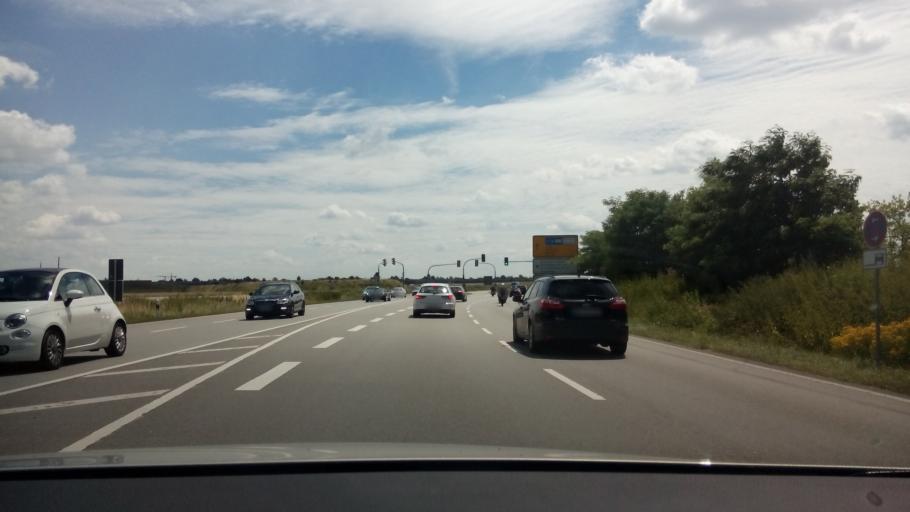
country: DE
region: Bavaria
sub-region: Upper Bavaria
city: Garching bei Munchen
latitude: 48.2489
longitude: 11.6331
